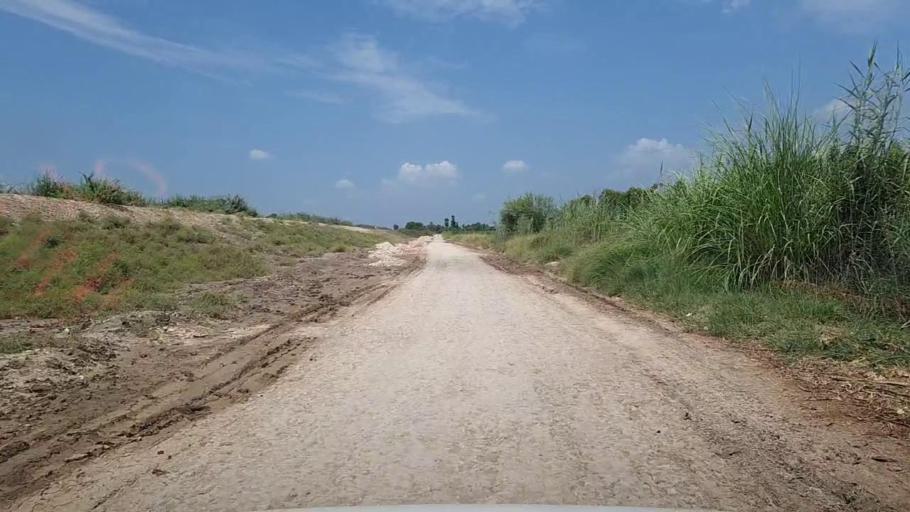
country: PK
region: Sindh
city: Bhiria
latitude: 26.9081
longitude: 68.2021
